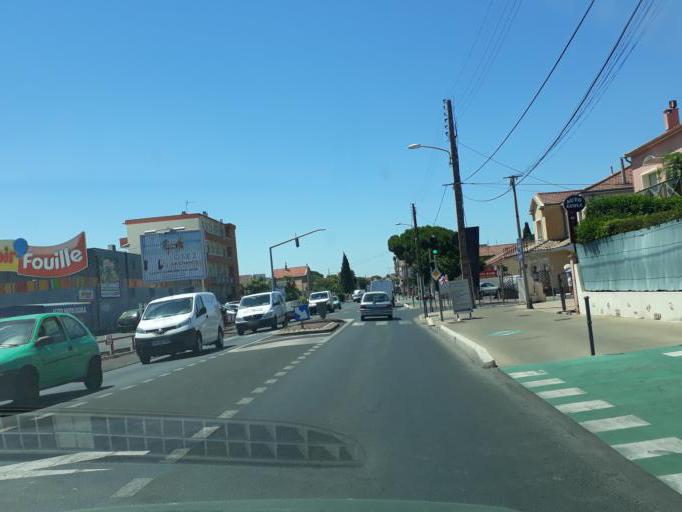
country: FR
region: Languedoc-Roussillon
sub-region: Departement de l'Herault
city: Agde
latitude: 43.3110
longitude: 3.4807
